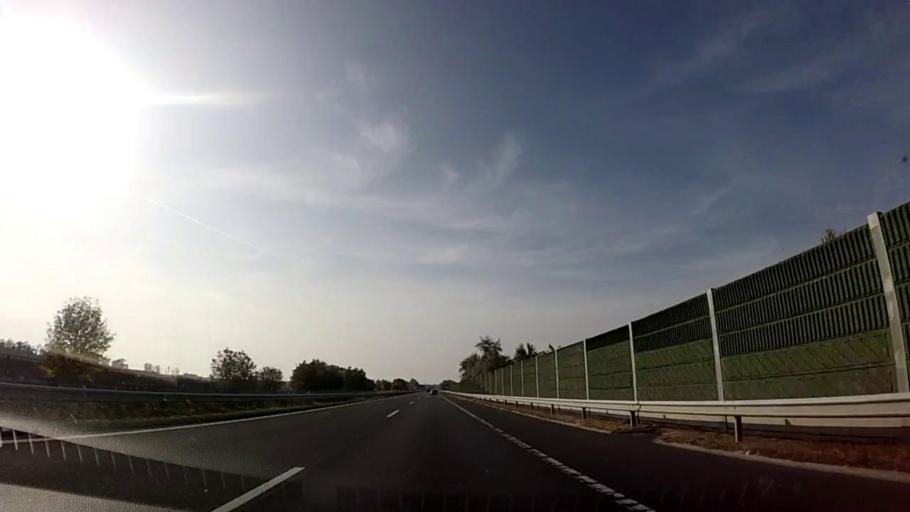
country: HU
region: Somogy
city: Balatonszabadi
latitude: 46.9470
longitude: 18.1499
